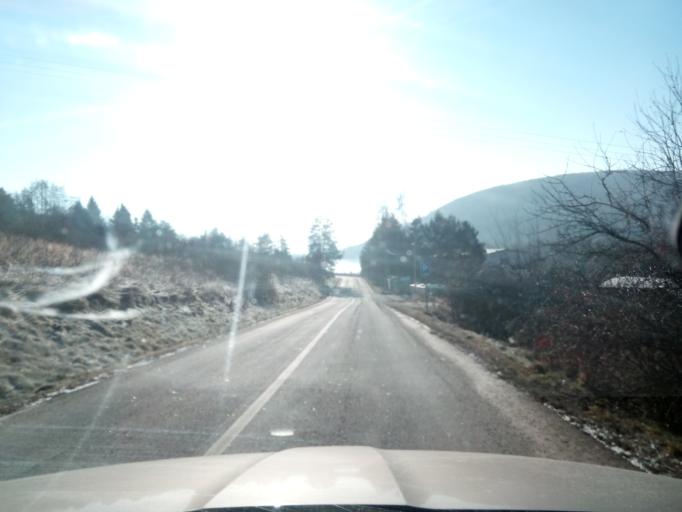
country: SK
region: Kosicky
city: Kosice
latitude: 48.7079
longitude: 21.1542
